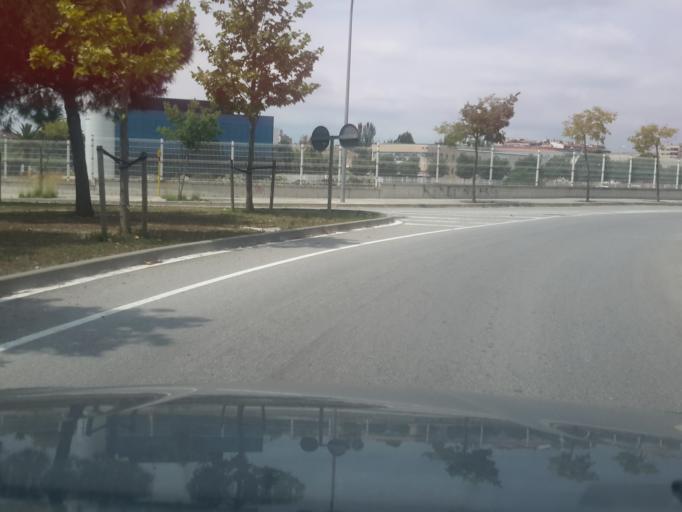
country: ES
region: Catalonia
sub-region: Provincia de Barcelona
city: Vilafranca del Penedes
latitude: 41.3489
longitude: 1.7136
